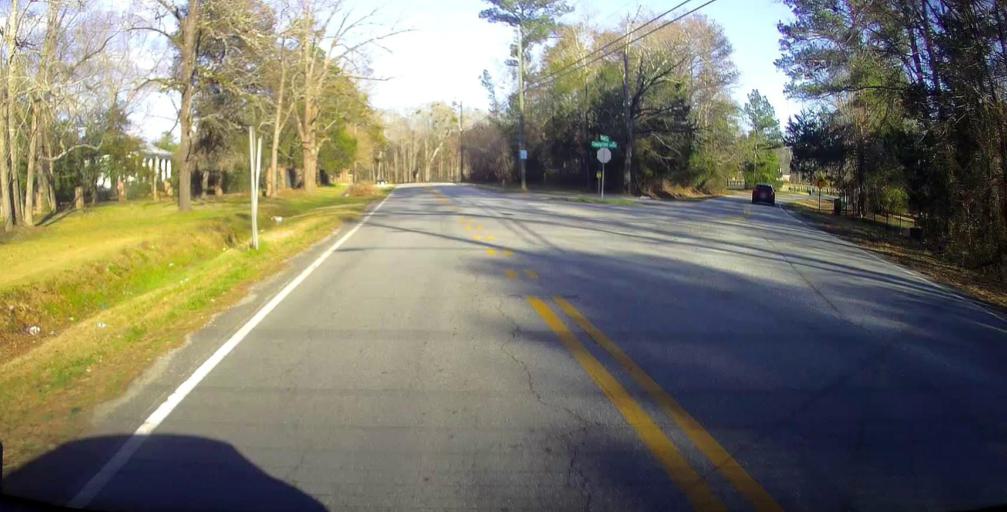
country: US
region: Georgia
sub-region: Harris County
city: Hamilton
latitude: 32.5762
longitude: -84.8130
